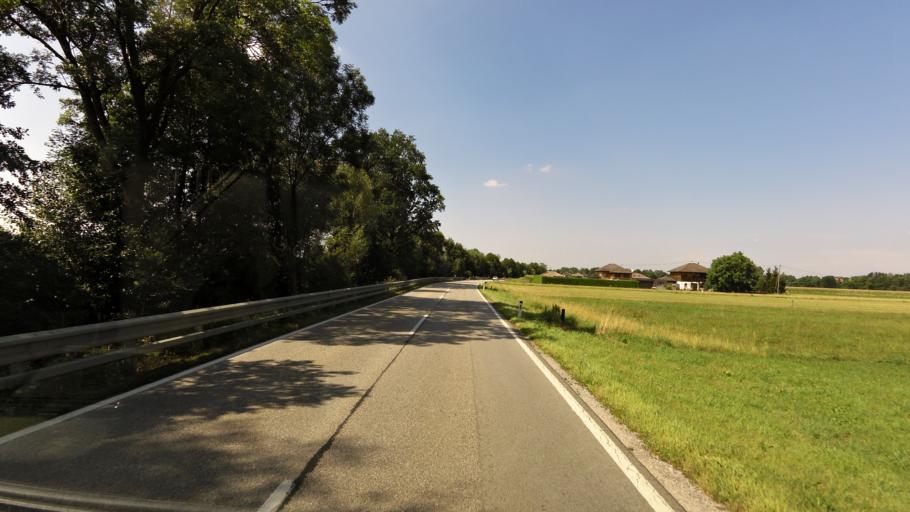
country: AT
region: Upper Austria
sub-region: Politischer Bezirk Braunau am Inn
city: Altheim
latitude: 48.1245
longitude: 13.1491
